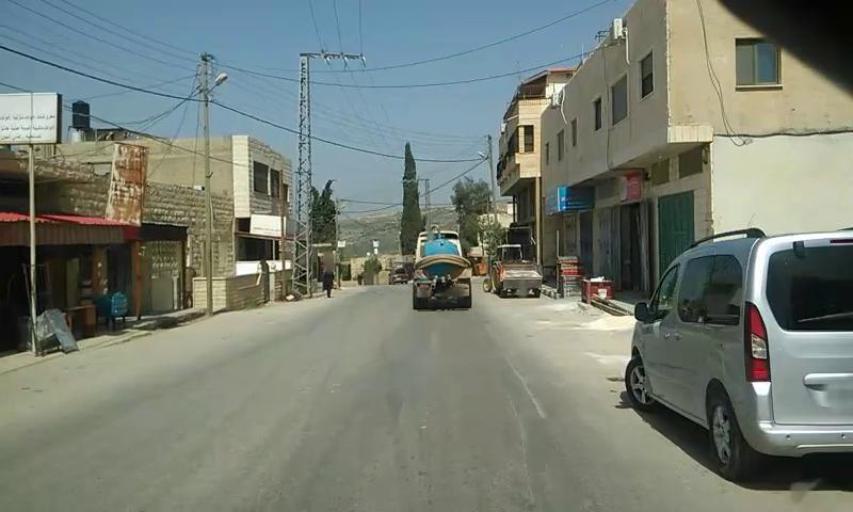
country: PS
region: West Bank
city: Az Zababidah
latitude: 32.3879
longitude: 35.3227
